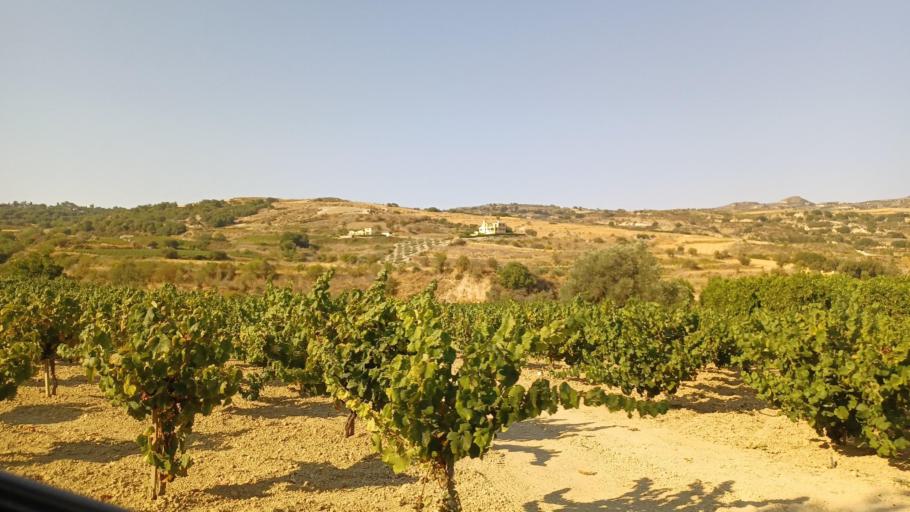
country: CY
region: Pafos
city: Tala
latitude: 34.9094
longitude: 32.4843
